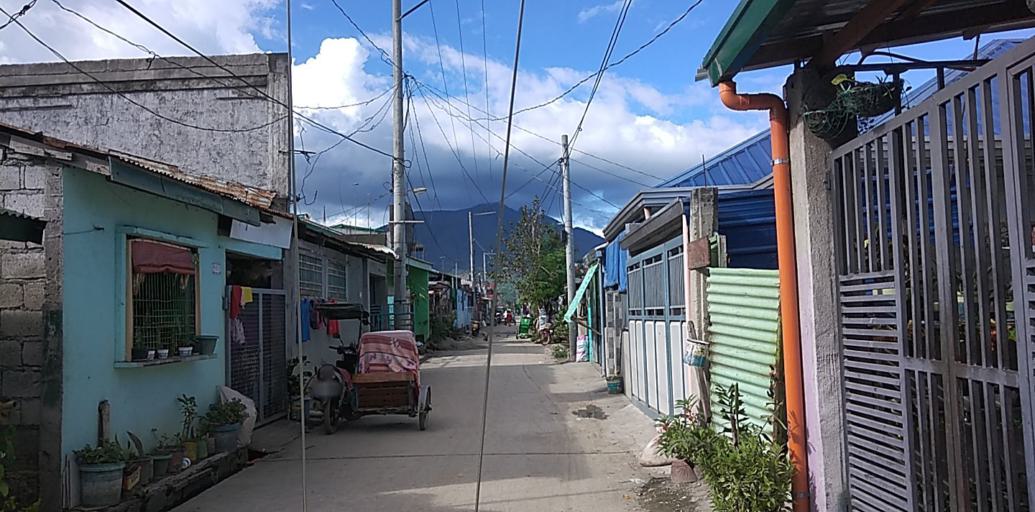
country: PH
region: Central Luzon
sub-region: Province of Pampanga
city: Arayat
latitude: 15.1373
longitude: 120.7707
